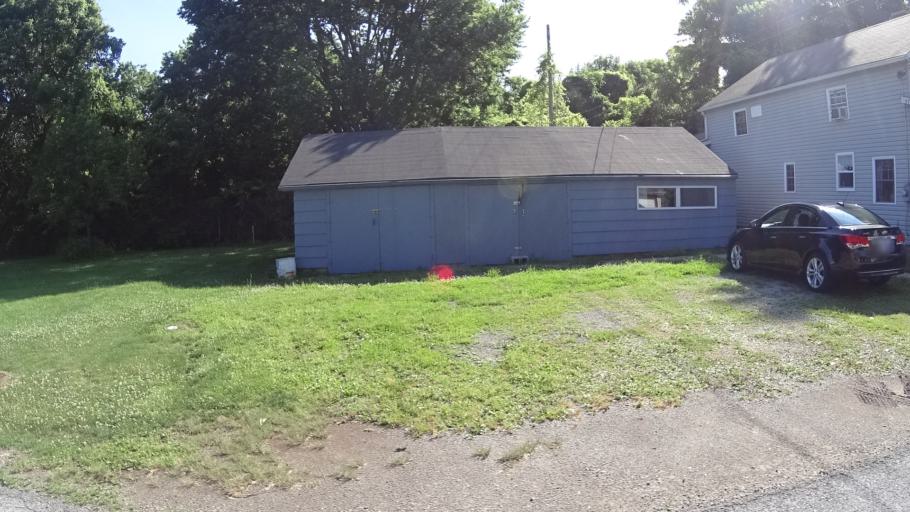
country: US
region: Ohio
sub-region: Erie County
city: Sandusky
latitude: 41.4710
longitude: -82.8109
